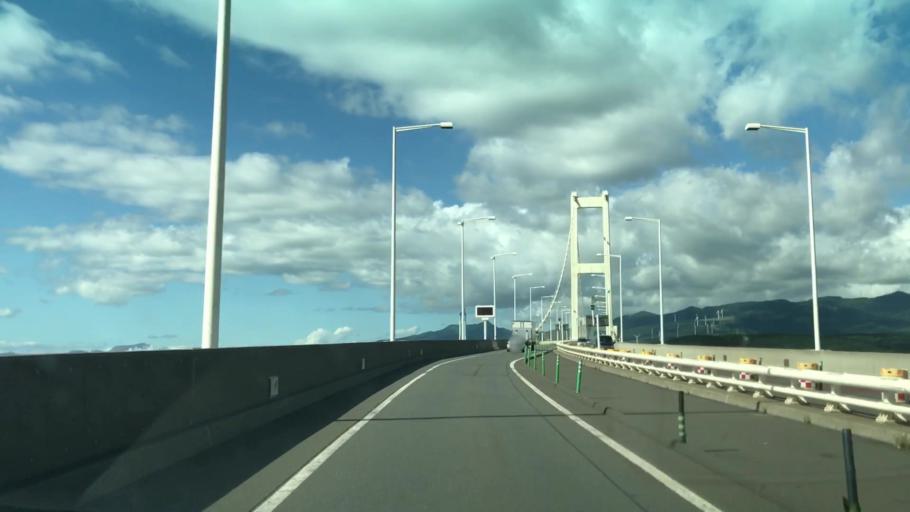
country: JP
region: Hokkaido
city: Muroran
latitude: 42.3451
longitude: 140.9490
